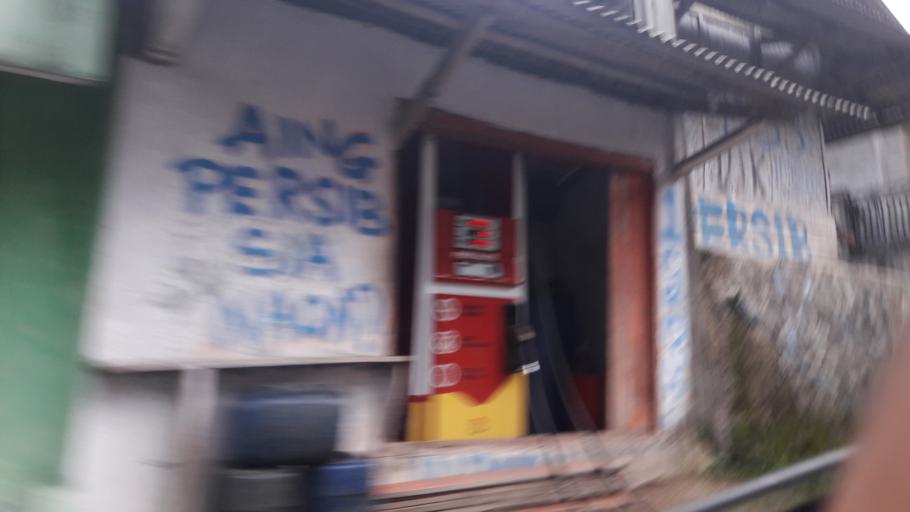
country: ID
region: West Java
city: Cipeundeuy
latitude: -6.6778
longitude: 106.5286
